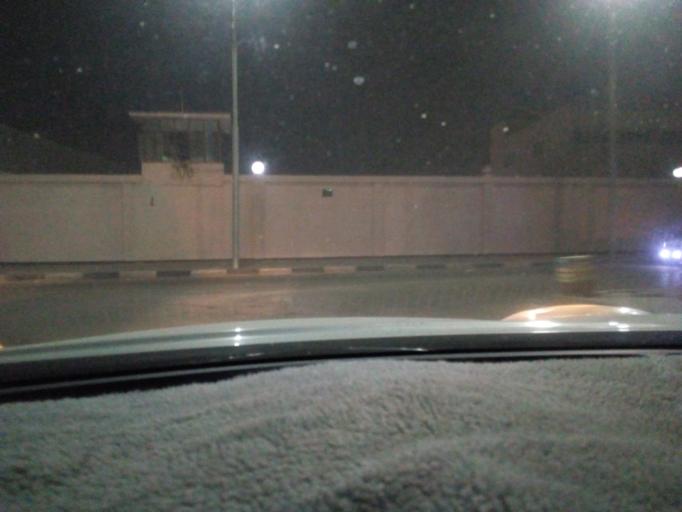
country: EG
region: Muhafazat al Qahirah
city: Cairo
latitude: 30.0915
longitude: 31.3431
